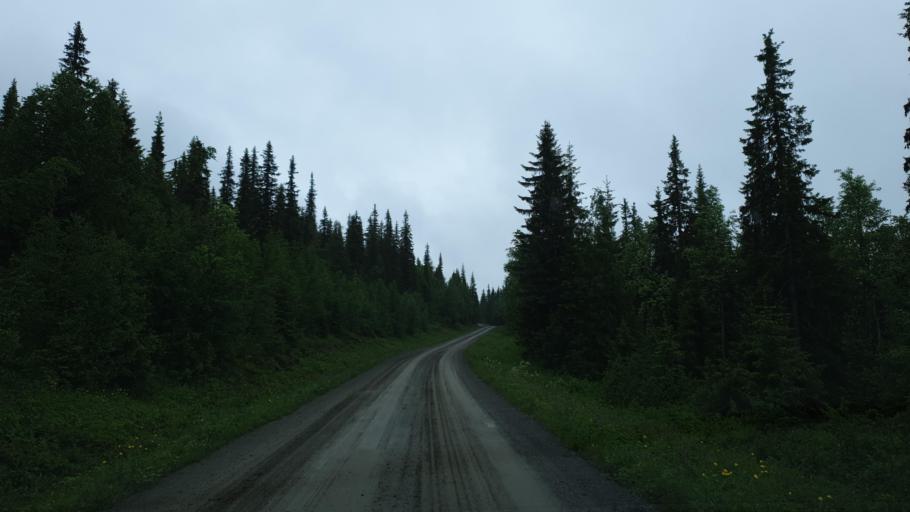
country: SE
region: Vaesterbotten
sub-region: Vilhelmina Kommun
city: Sjoberg
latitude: 65.3323
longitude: 15.9048
